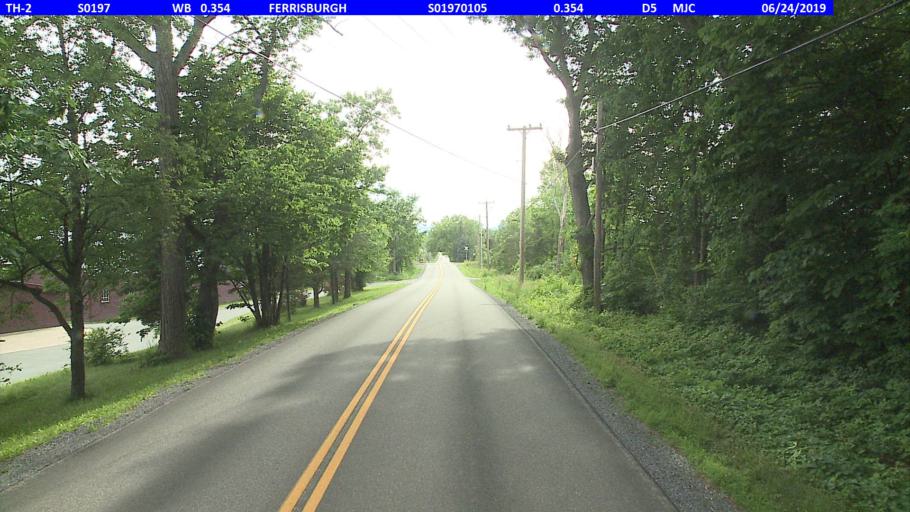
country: US
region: Vermont
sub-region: Addison County
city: Vergennes
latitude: 44.1729
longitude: -73.2320
